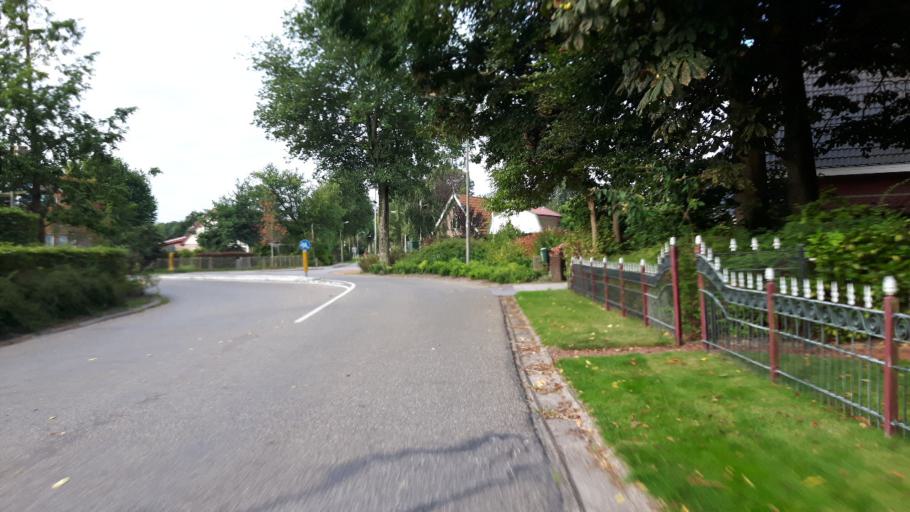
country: NL
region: North Holland
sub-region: Gemeente Hoorn
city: Hoorn
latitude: 52.6954
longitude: 5.0523
